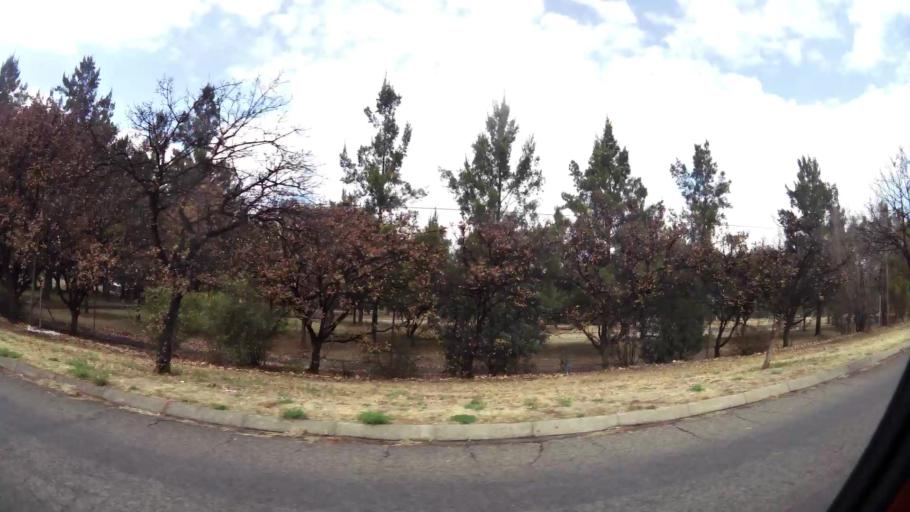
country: ZA
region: Gauteng
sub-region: Sedibeng District Municipality
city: Vanderbijlpark
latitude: -26.7426
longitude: 27.8497
